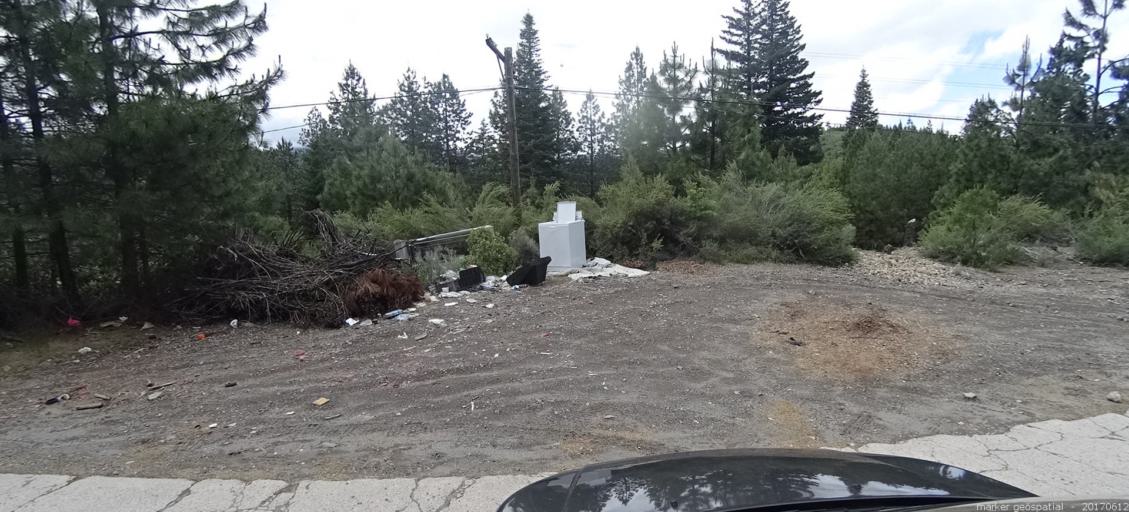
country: US
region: California
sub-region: Siskiyou County
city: Weed
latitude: 41.3810
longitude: -122.3727
